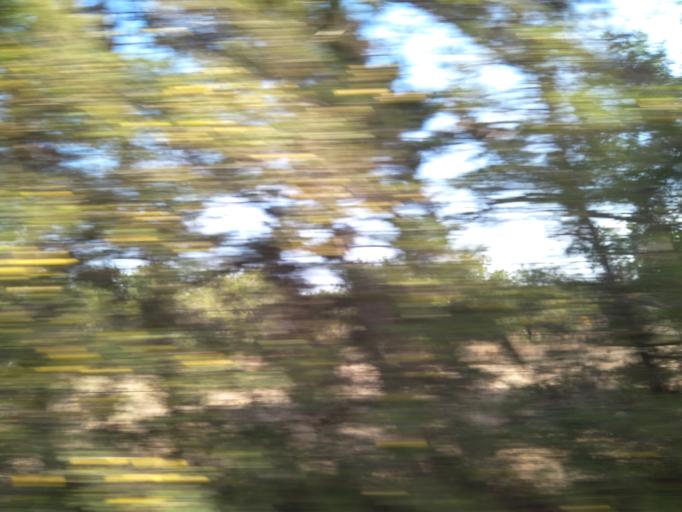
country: PT
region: Faro
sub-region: Faro
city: Santa Barbara de Nexe
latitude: 37.0622
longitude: -7.9549
